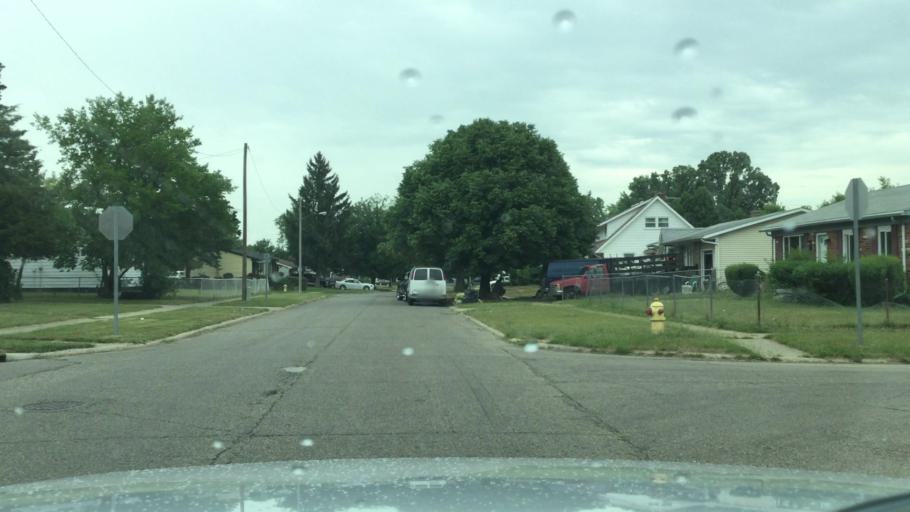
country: US
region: Michigan
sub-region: Genesee County
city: Beecher
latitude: 43.0699
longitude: -83.7195
